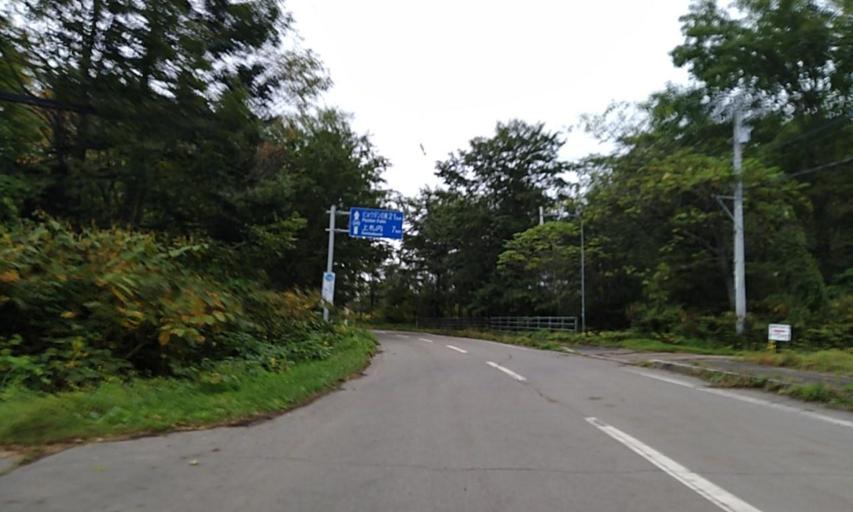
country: JP
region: Hokkaido
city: Obihiro
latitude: 42.6705
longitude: 143.0395
